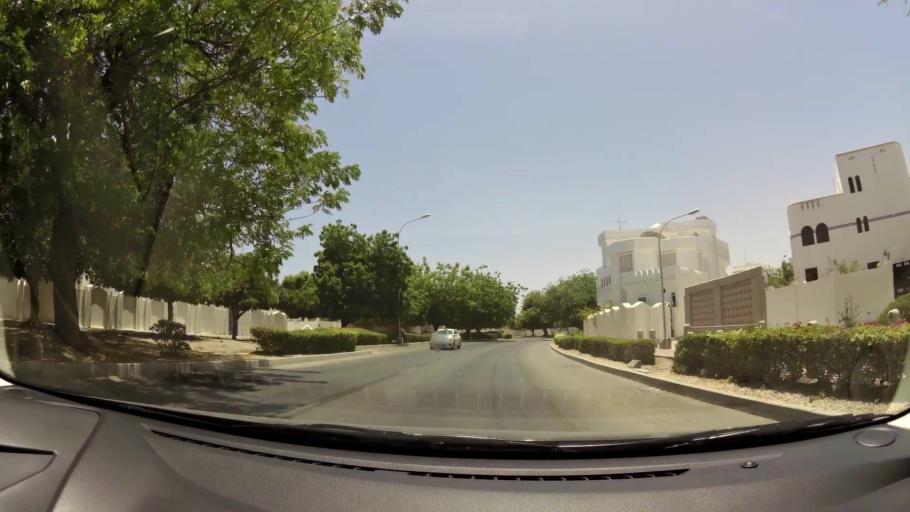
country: OM
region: Muhafazat Masqat
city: Bawshar
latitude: 23.6088
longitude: 58.4507
